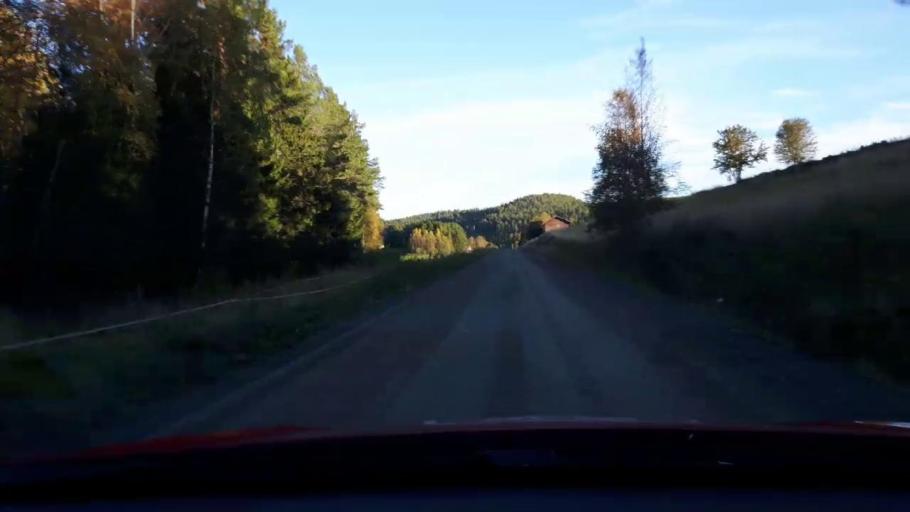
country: SE
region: Jaemtland
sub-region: OEstersunds Kommun
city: Brunflo
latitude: 62.9231
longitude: 15.0104
